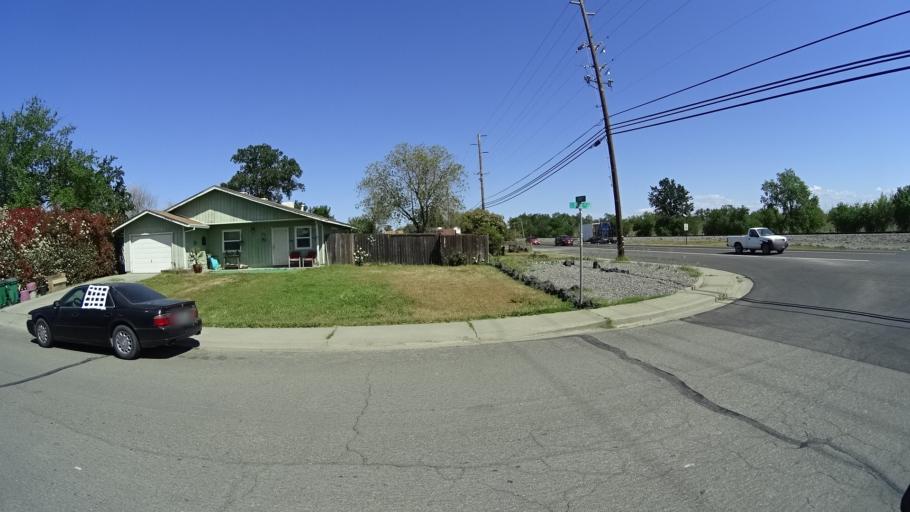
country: US
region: California
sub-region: Glenn County
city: Orland
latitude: 39.7569
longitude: -122.1973
